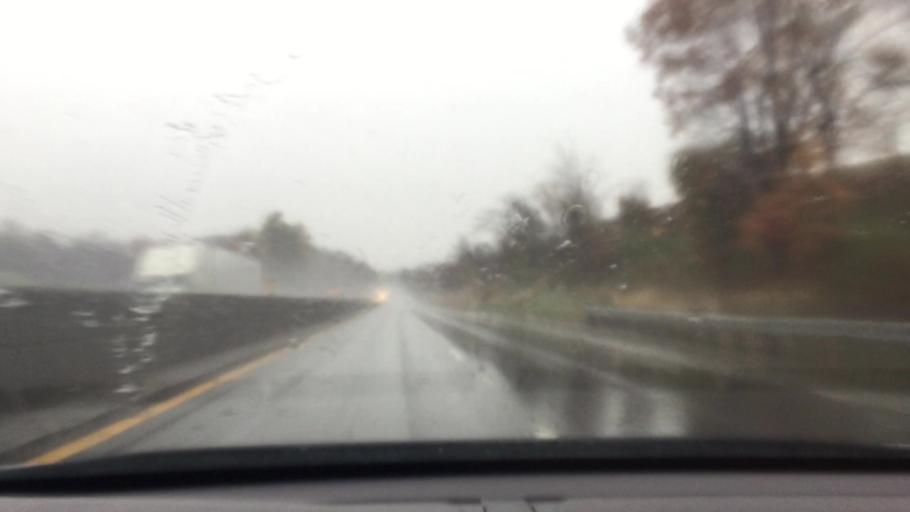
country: US
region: Pennsylvania
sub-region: Washington County
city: Ellsworth
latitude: 40.1675
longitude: -80.0894
